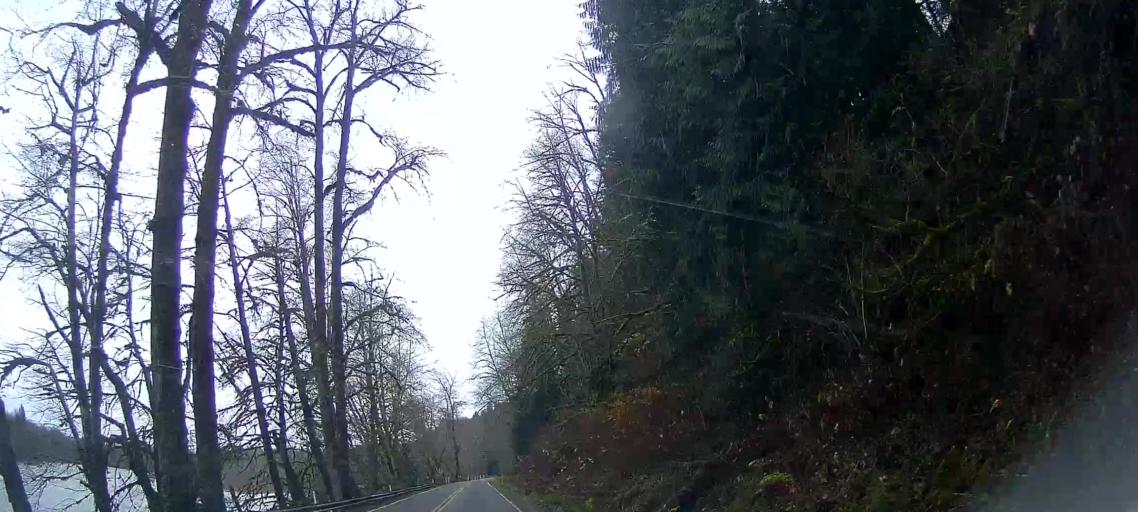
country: US
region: Washington
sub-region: Skagit County
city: Sedro-Woolley
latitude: 48.5100
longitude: -121.9009
